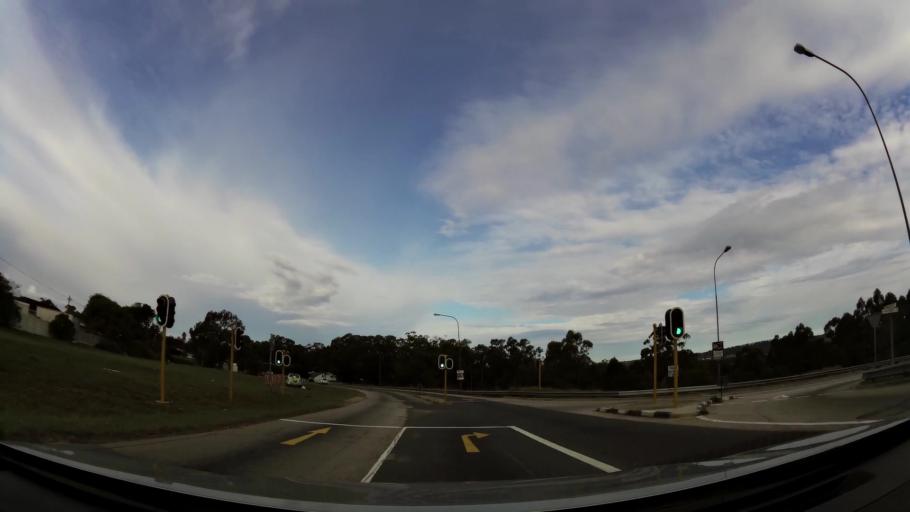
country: ZA
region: Eastern Cape
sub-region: Nelson Mandela Bay Metropolitan Municipality
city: Port Elizabeth
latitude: -33.9524
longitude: 25.5125
